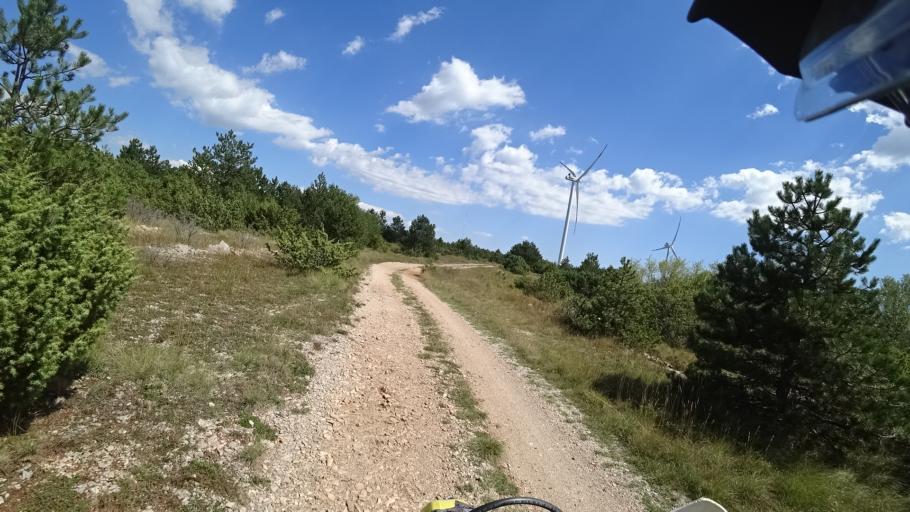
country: HR
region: Splitsko-Dalmatinska
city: Hrvace
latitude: 43.7192
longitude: 16.5245
